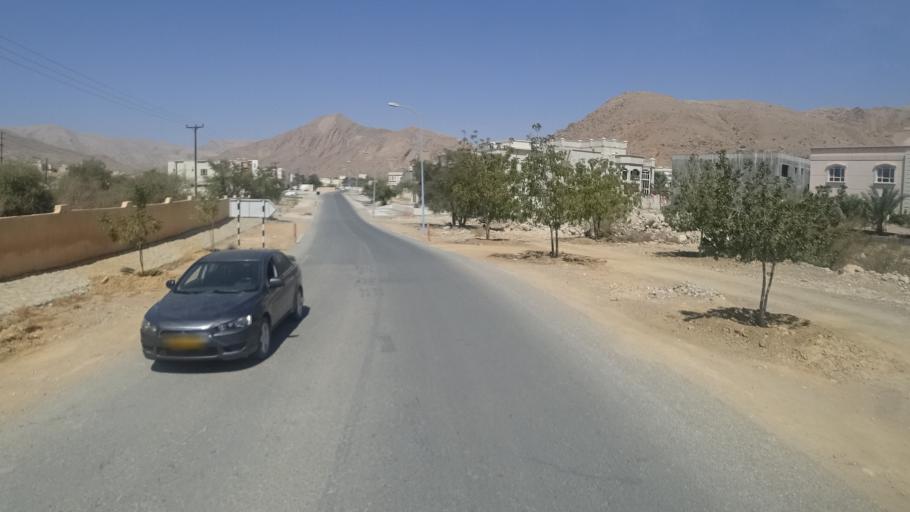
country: OM
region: Ash Sharqiyah
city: Badiyah
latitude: 22.5871
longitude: 59.0910
